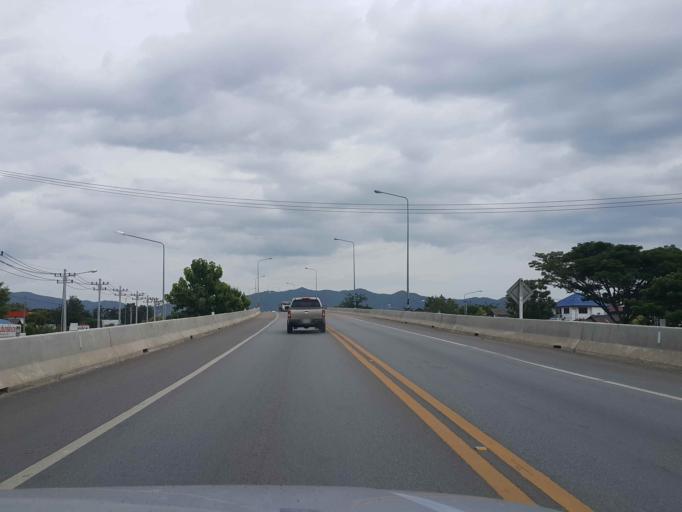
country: TH
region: Lampang
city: Lampang
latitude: 18.2524
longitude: 99.4884
